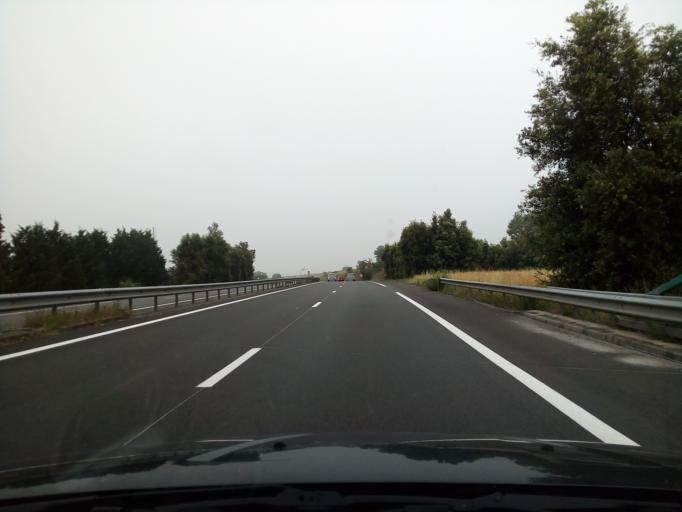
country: FR
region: Poitou-Charentes
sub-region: Departement de la Charente
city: Gensac-la-Pallue
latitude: 45.6646
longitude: -0.2320
